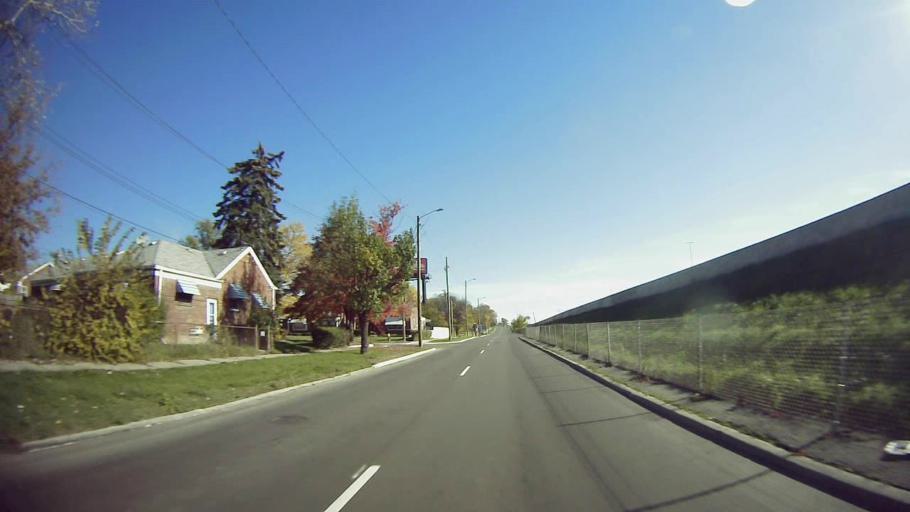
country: US
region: Michigan
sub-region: Wayne County
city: Redford
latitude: 42.3861
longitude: -83.2642
